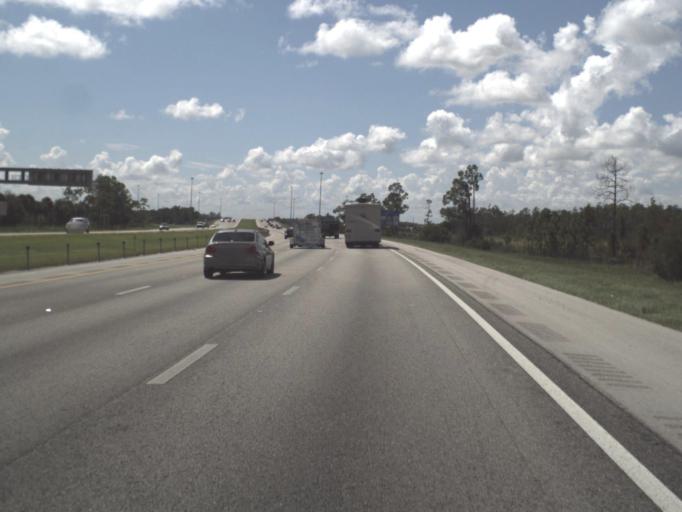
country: US
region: Florida
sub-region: Lee County
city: Fort Myers
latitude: 26.6216
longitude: -81.8058
